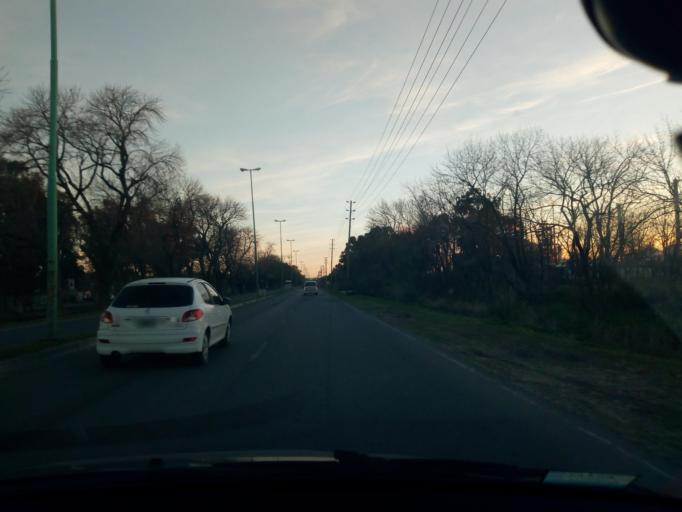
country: AR
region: Buenos Aires
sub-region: Partido de Ensenada
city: Ensenada
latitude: -34.8732
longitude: -57.9148
